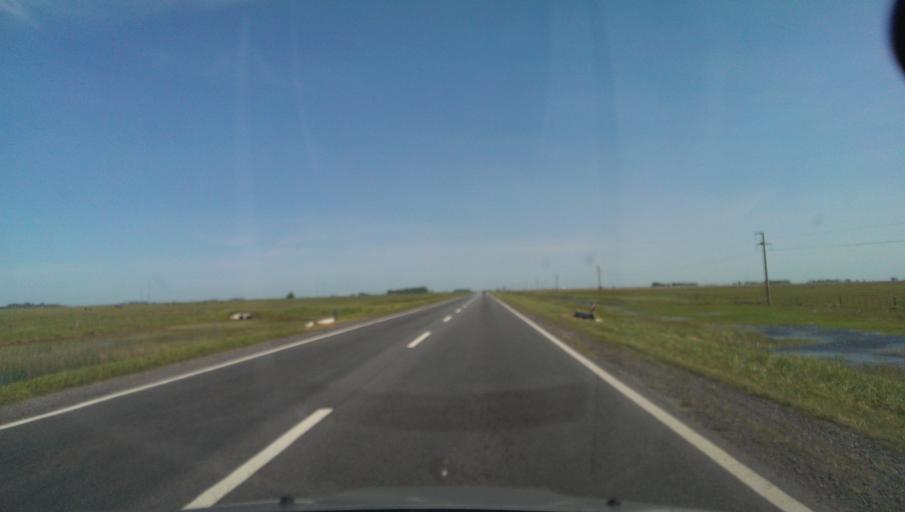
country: AR
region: Buenos Aires
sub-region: Partido de Azul
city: Azul
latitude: -36.5711
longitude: -59.6413
